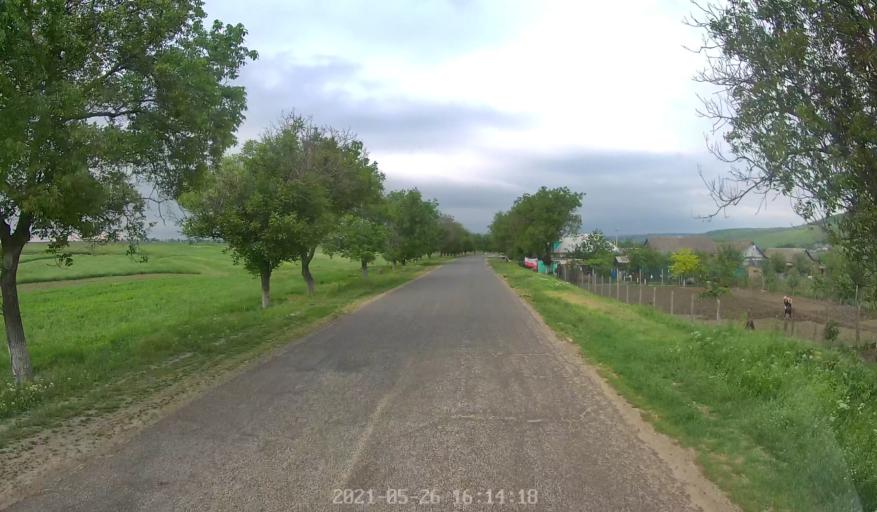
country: MD
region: Hincesti
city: Dancu
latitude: 46.7086
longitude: 28.3409
